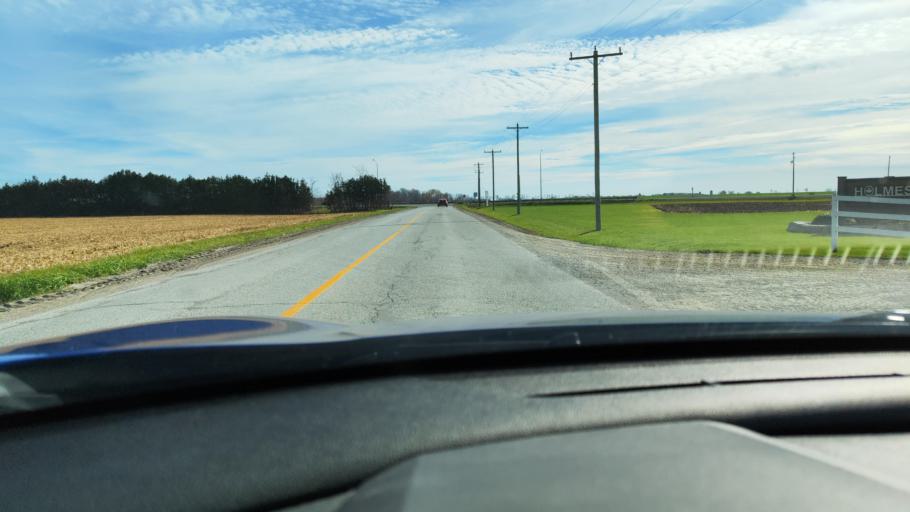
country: CA
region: Ontario
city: Wasaga Beach
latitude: 44.4389
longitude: -79.9973
